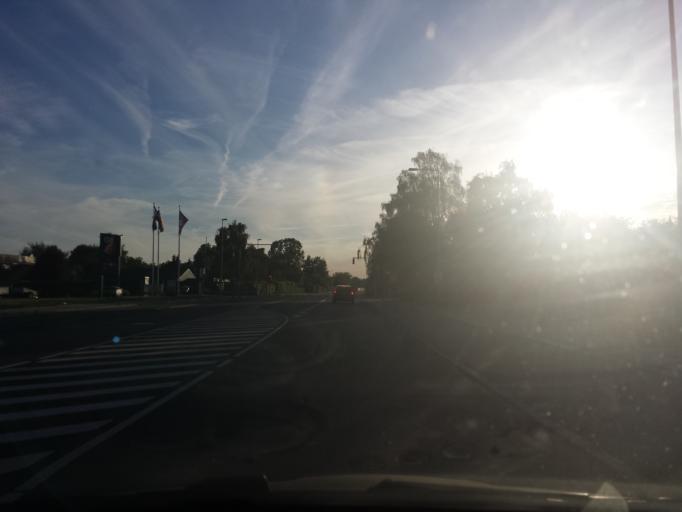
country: DK
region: Capital Region
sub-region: Egedal Kommune
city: Stenlose
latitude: 55.7678
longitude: 12.1863
